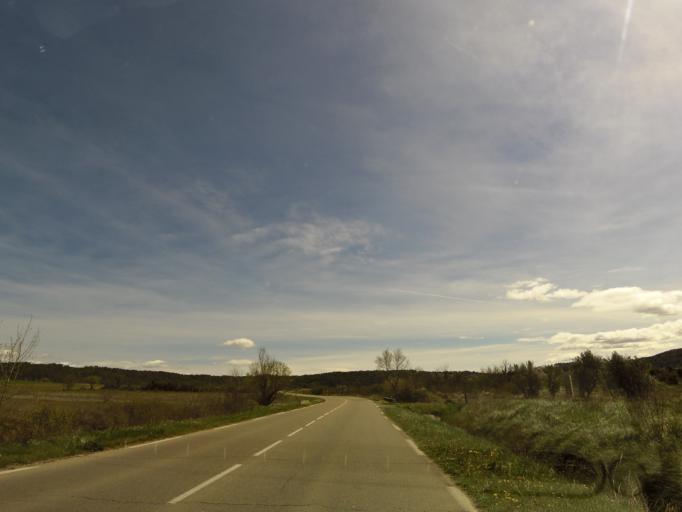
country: FR
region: Languedoc-Roussillon
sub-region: Departement du Gard
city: Clarensac
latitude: 43.8170
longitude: 4.2360
